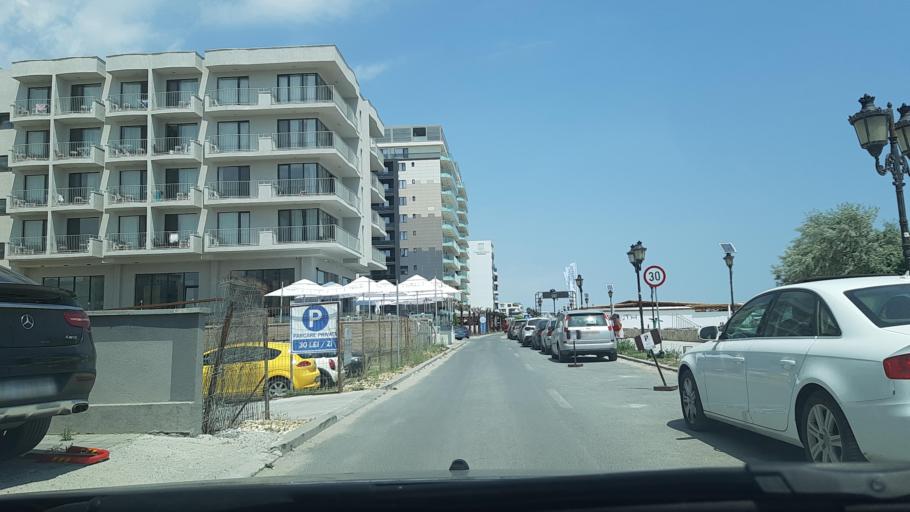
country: RO
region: Constanta
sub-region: Comuna Navodari
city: Navodari
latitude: 44.2927
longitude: 28.6238
